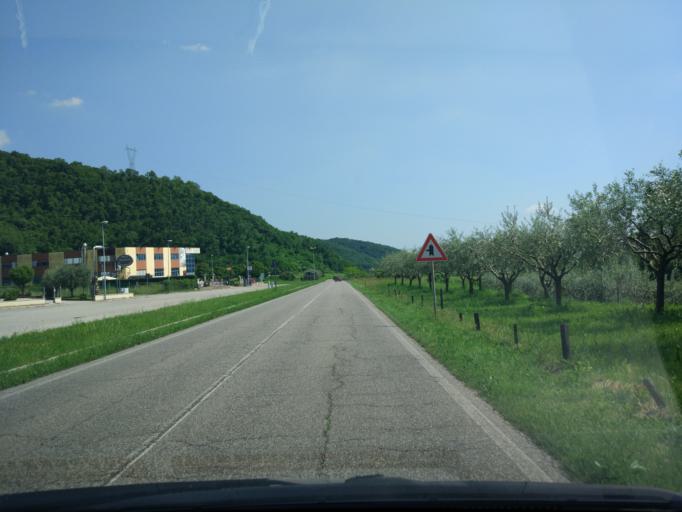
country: IT
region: Veneto
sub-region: Provincia di Verona
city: Tregnago
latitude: 45.5369
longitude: 11.1567
